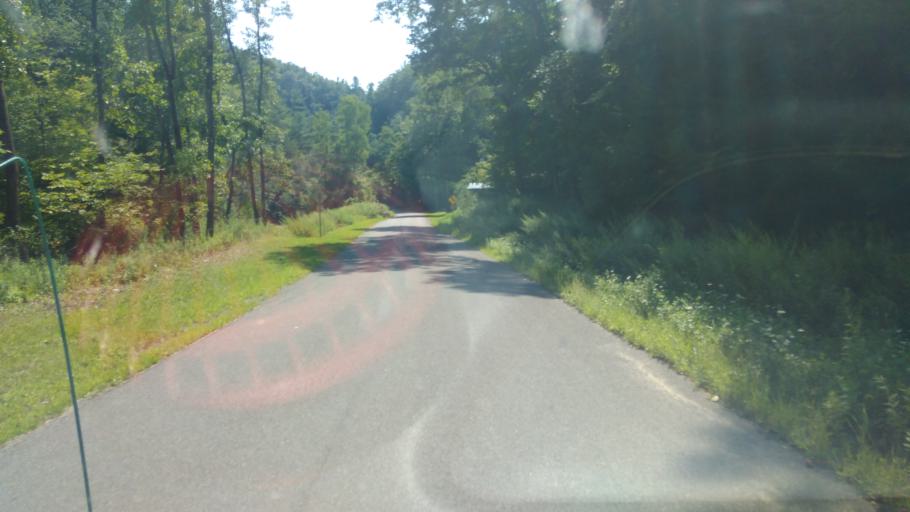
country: US
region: New York
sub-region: Steuben County
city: Canisteo
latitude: 42.2976
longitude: -77.6128
